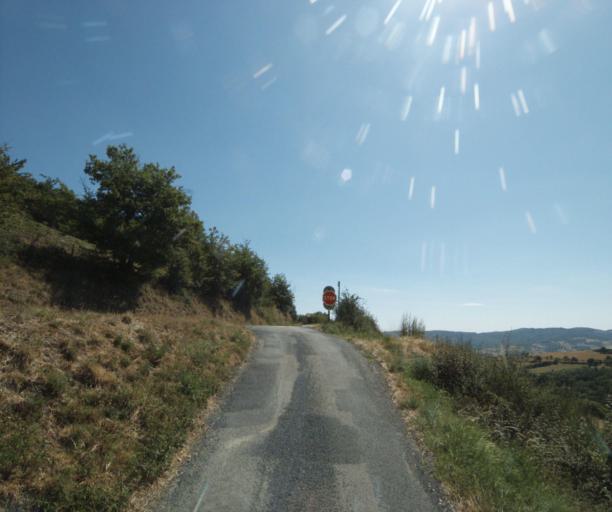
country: FR
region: Rhone-Alpes
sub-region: Departement du Rhone
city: Bessenay
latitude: 45.7930
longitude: 4.5302
